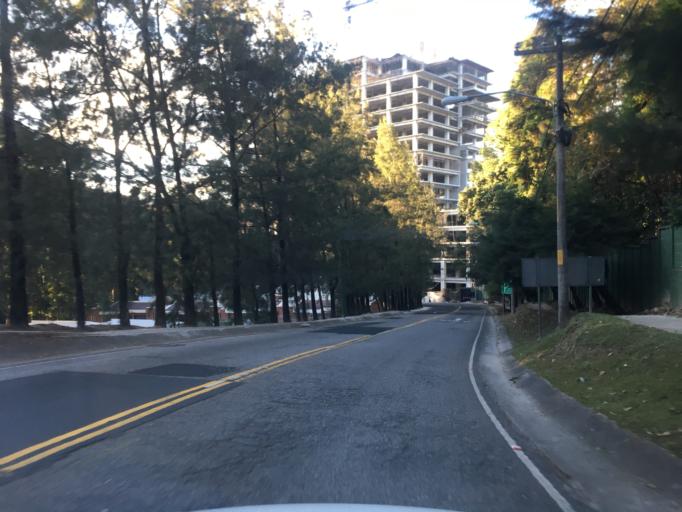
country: GT
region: Guatemala
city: Santa Catarina Pinula
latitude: 14.6042
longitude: -90.4931
